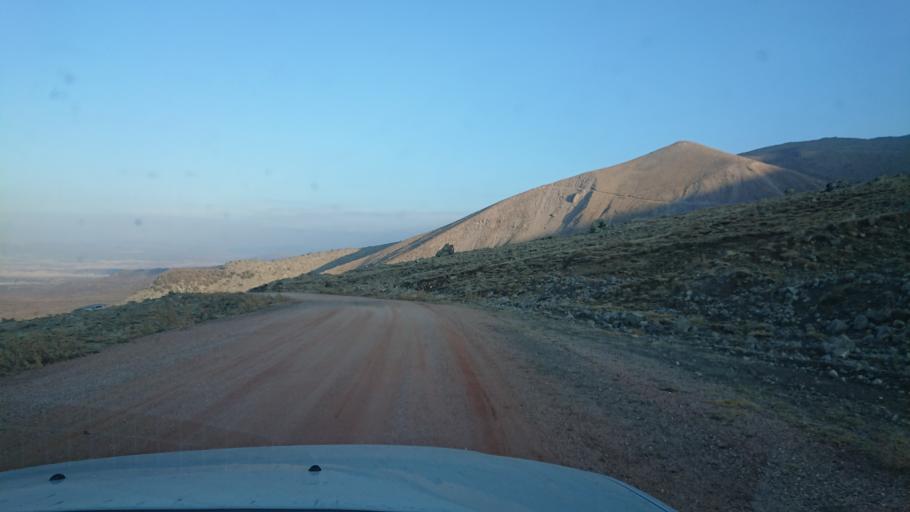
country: TR
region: Aksaray
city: Taspinar
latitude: 38.1591
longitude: 34.1702
